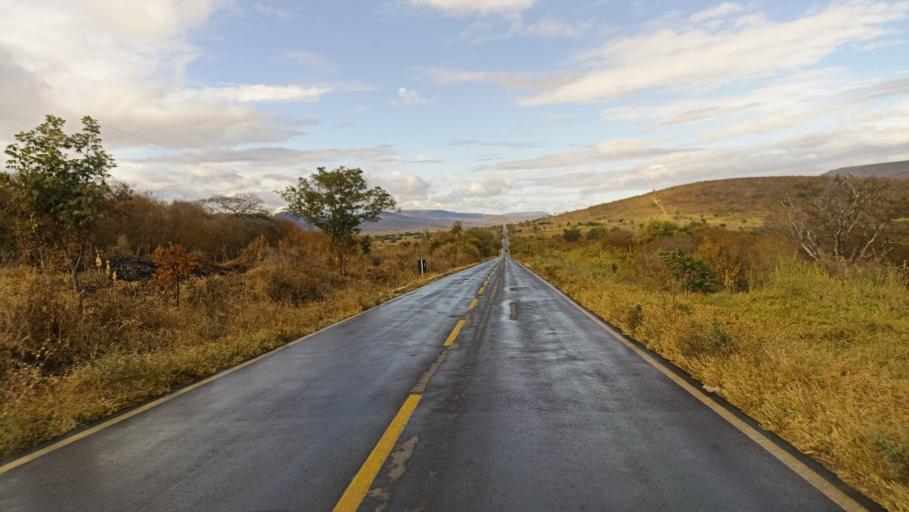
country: BR
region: Minas Gerais
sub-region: Itinga
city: Itinga
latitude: -16.5895
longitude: -41.6793
